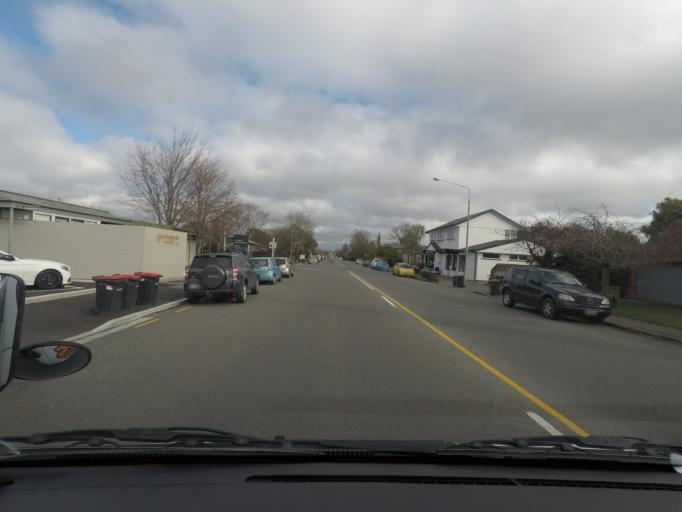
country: NZ
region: Canterbury
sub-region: Christchurch City
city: Christchurch
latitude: -43.5092
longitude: 172.6306
